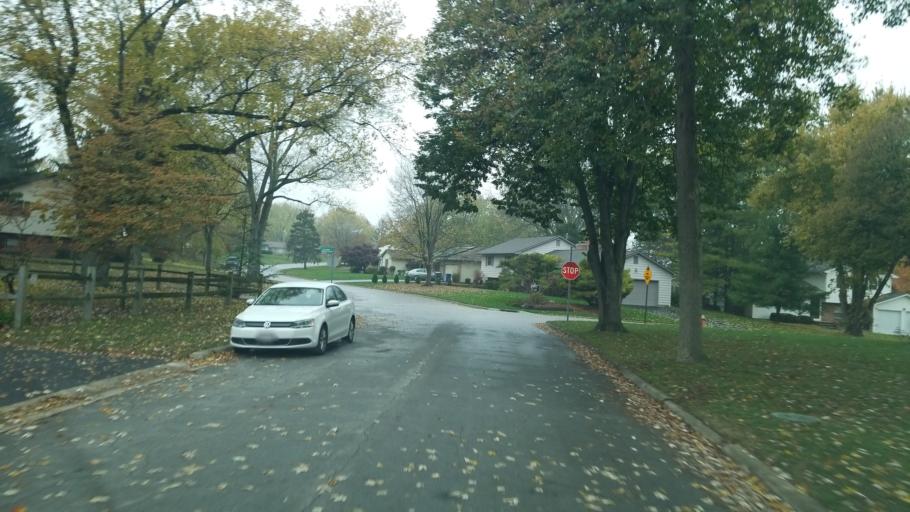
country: US
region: Ohio
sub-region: Franklin County
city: Worthington
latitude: 40.0473
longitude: -83.0454
